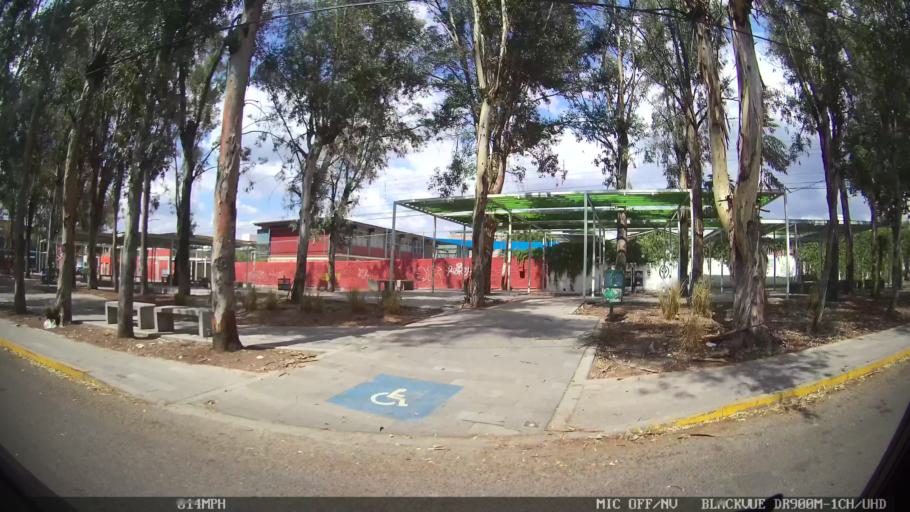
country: MX
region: Jalisco
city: Tlaquepaque
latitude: 20.6846
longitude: -103.2641
